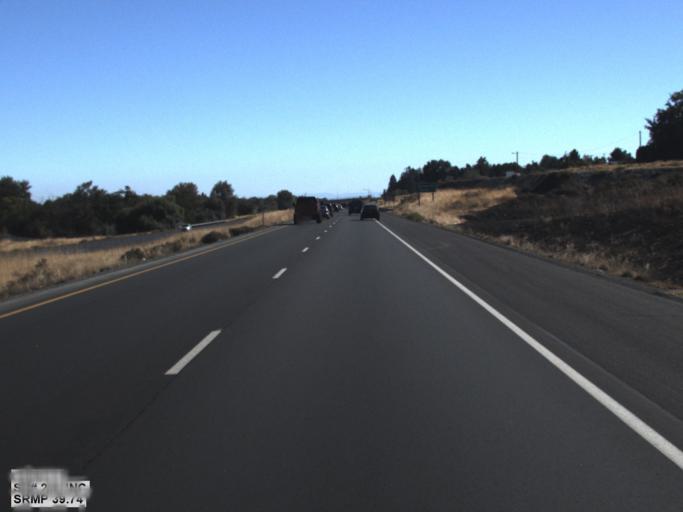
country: US
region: Washington
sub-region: Franklin County
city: West Pasco
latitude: 46.2311
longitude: -119.2062
